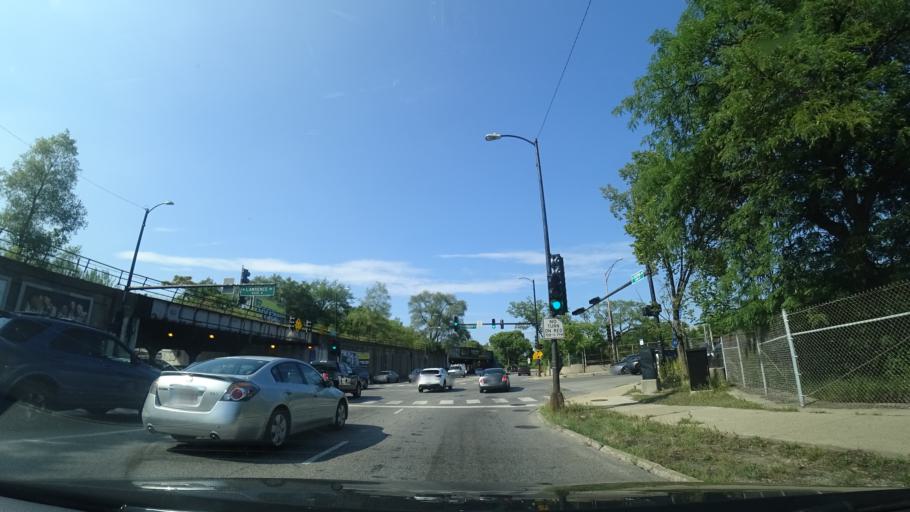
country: US
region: Illinois
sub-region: Cook County
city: Lincolnwood
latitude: 41.9678
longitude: -87.7477
